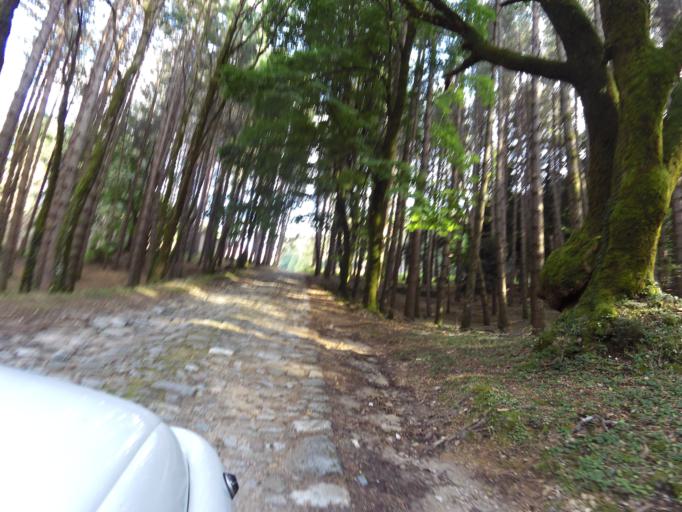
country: IT
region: Calabria
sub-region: Provincia di Vibo-Valentia
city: Nardodipace
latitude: 38.5091
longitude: 16.3781
